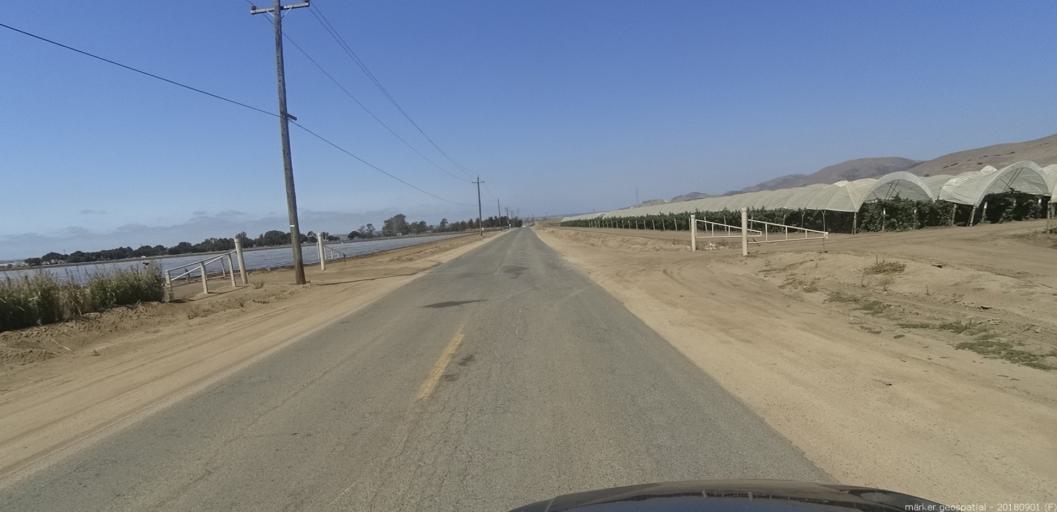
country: US
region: California
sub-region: Monterey County
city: Salinas
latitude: 36.6951
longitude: -121.5712
